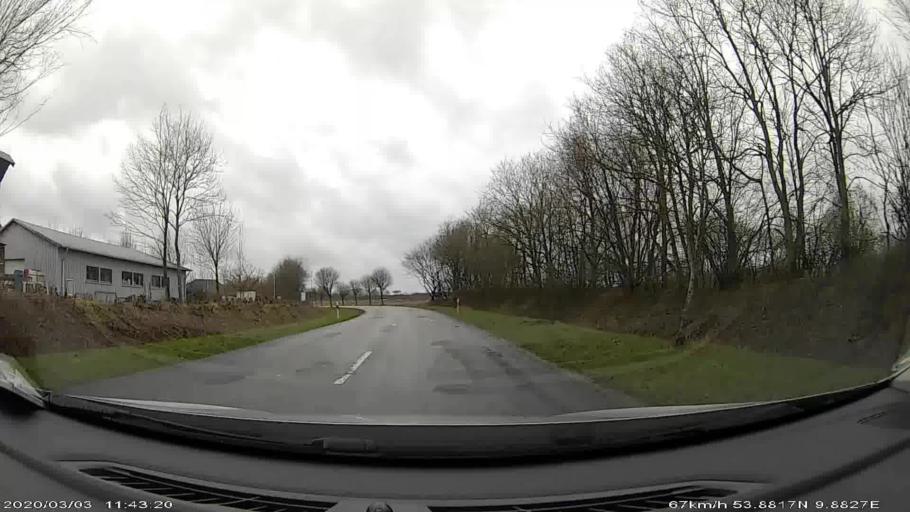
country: DE
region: Schleswig-Holstein
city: Lentfohrden
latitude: 53.8811
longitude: 9.8795
